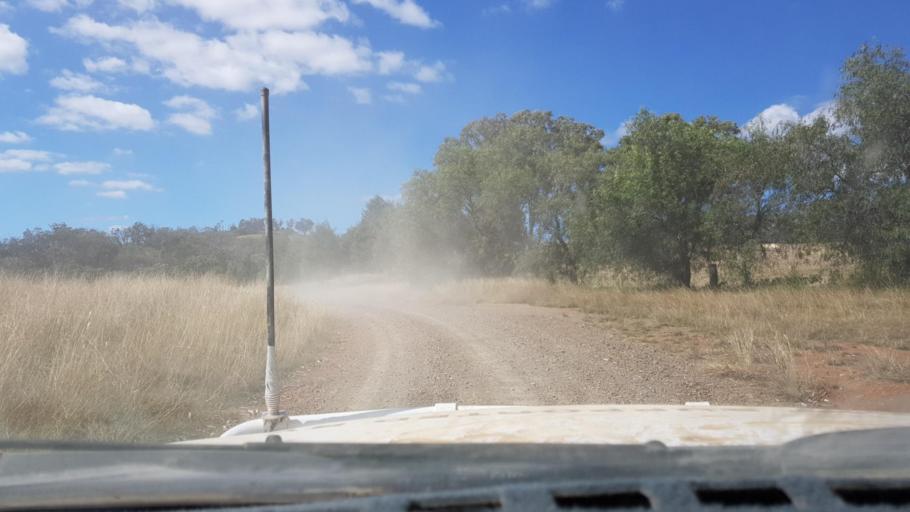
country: AU
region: New South Wales
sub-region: Tamworth Municipality
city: Manilla
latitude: -30.4302
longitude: 150.8201
